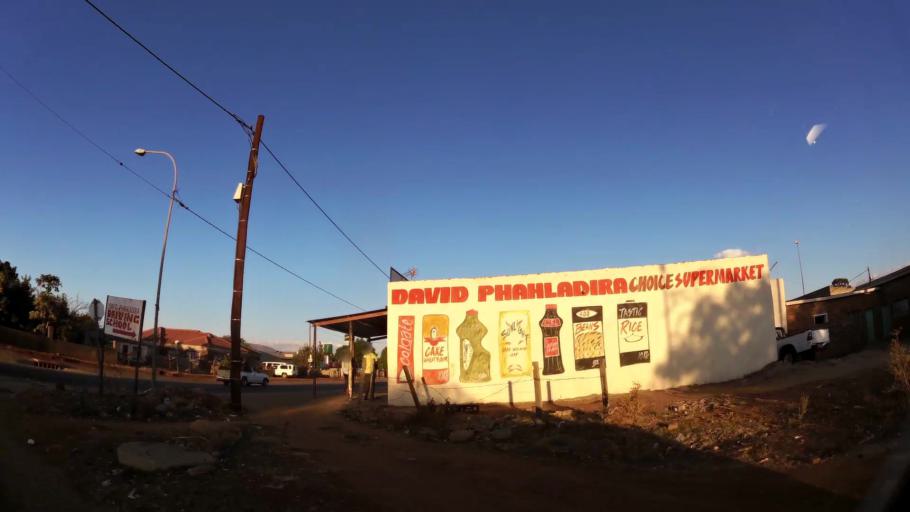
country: ZA
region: Limpopo
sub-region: Waterberg District Municipality
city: Mokopane
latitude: -24.1440
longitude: 28.9740
